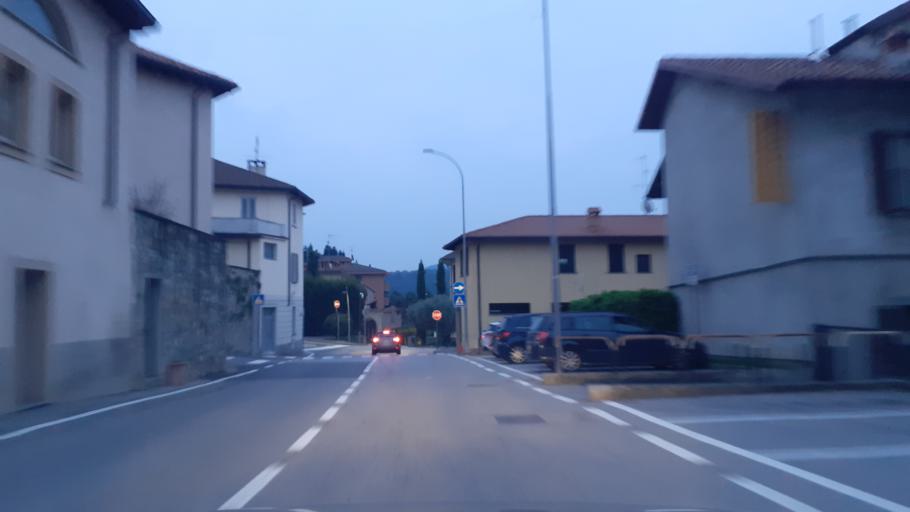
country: IT
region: Lombardy
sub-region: Provincia di Lecco
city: Bulciago
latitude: 45.7545
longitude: 9.2890
